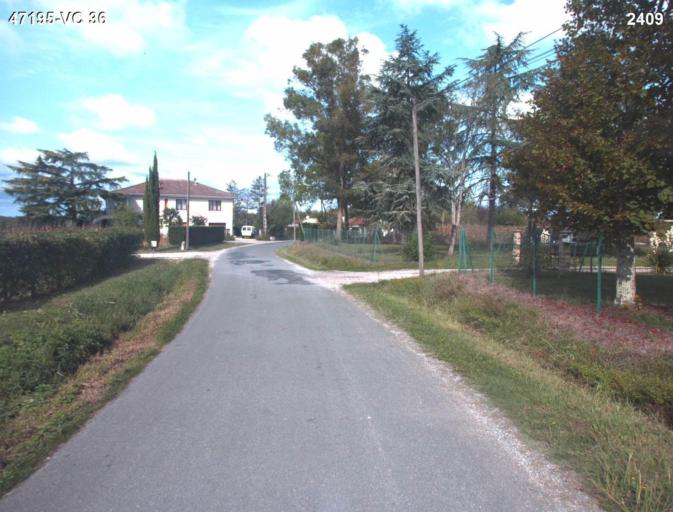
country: FR
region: Aquitaine
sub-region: Departement du Lot-et-Garonne
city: Nerac
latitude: 44.1278
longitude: 0.3246
